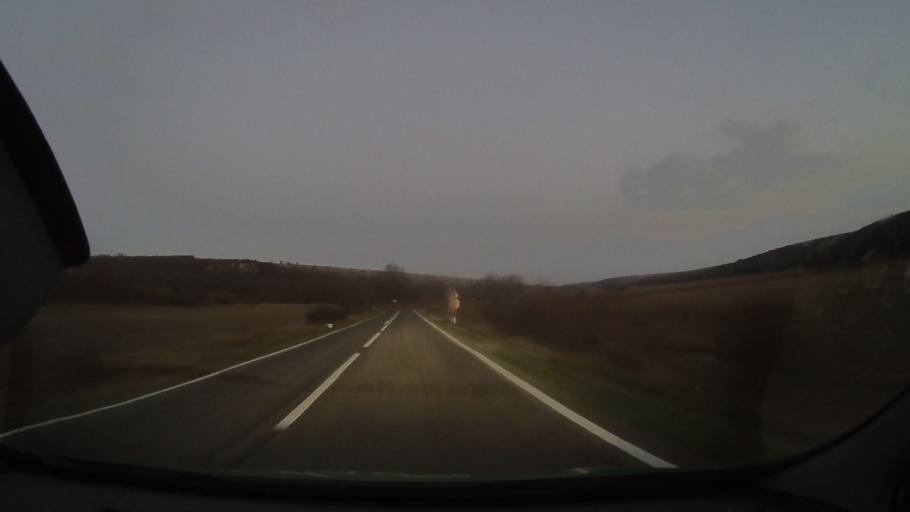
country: RO
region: Constanta
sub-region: Comuna Ion Corvin
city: Ion Corvin
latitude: 44.1101
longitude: 27.7730
